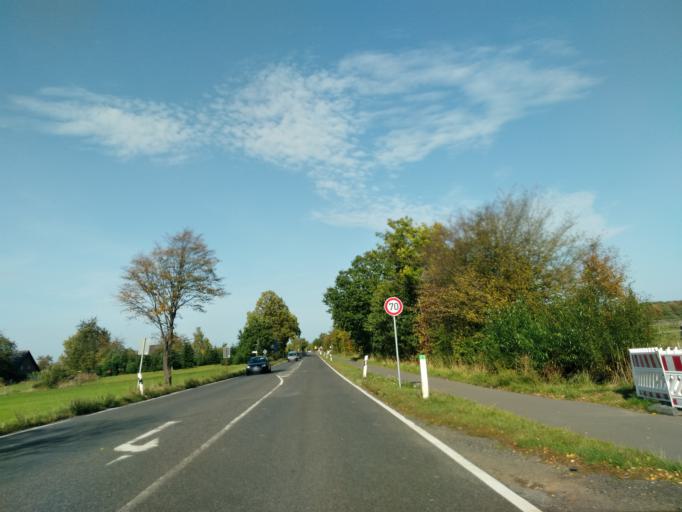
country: DE
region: North Rhine-Westphalia
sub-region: Regierungsbezirk Koln
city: Bad Honnef
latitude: 50.6912
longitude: 7.2769
